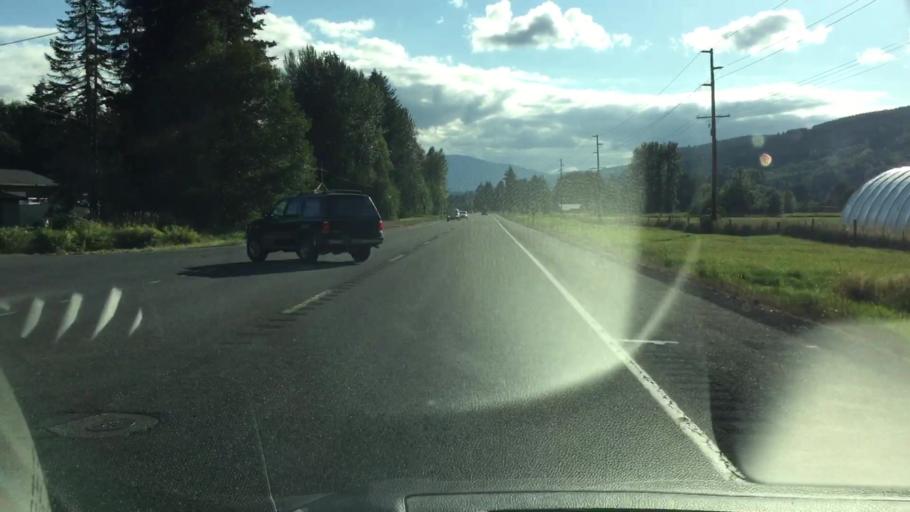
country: US
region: Washington
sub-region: Lewis County
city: Morton
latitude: 46.5281
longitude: -122.1367
